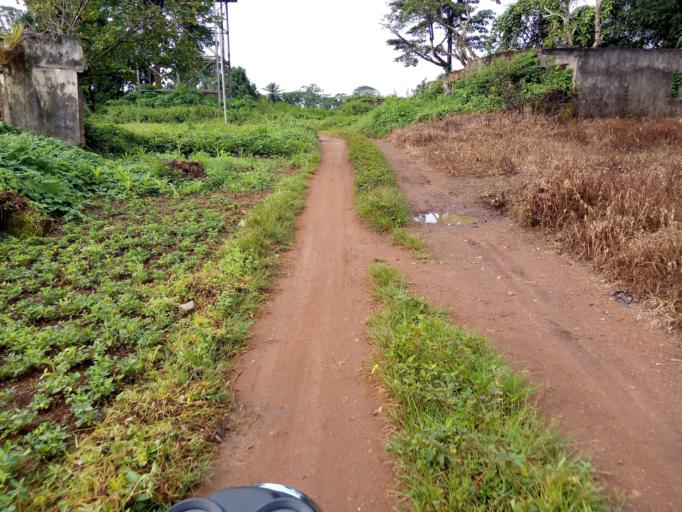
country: SL
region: Eastern Province
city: Buedu
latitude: 8.4630
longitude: -10.3408
